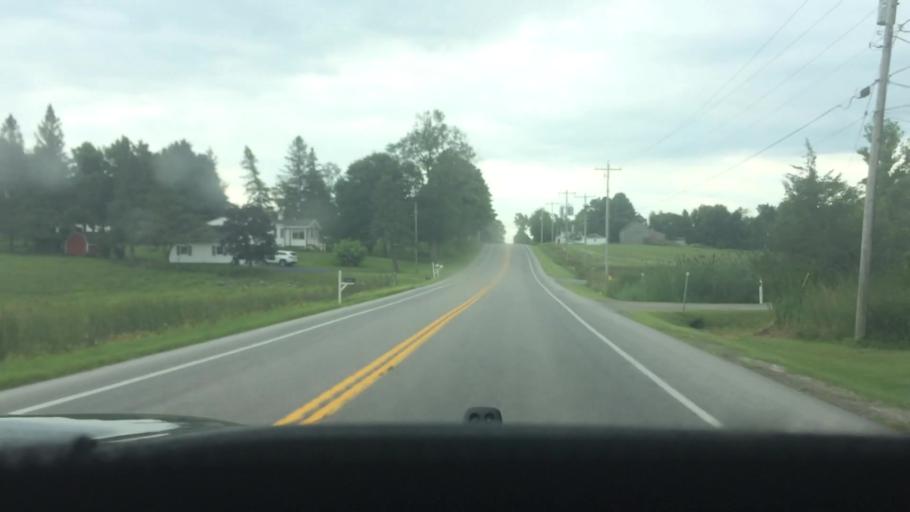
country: US
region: New York
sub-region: St. Lawrence County
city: Ogdensburg
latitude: 44.6113
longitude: -75.3987
